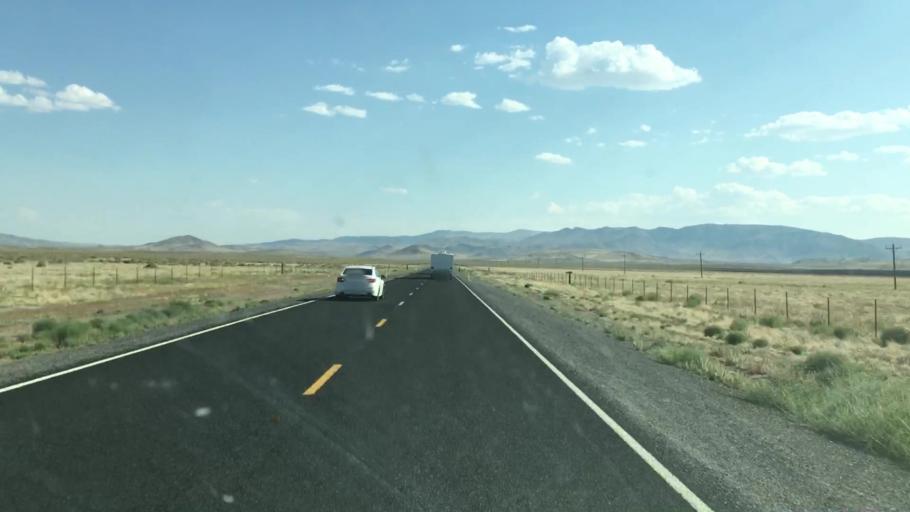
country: US
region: Nevada
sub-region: Lyon County
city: Fernley
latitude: 39.6816
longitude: -119.3347
